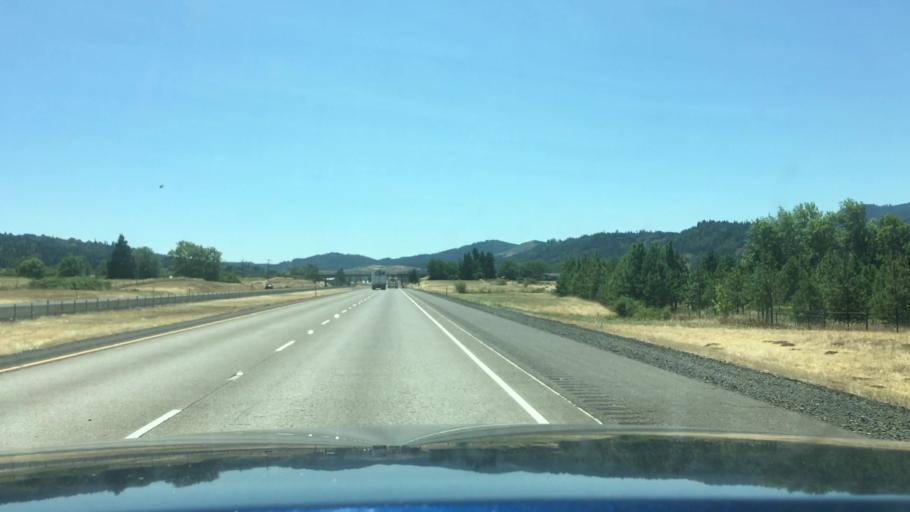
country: US
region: Oregon
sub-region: Douglas County
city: Yoncalla
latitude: 43.5840
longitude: -123.2578
